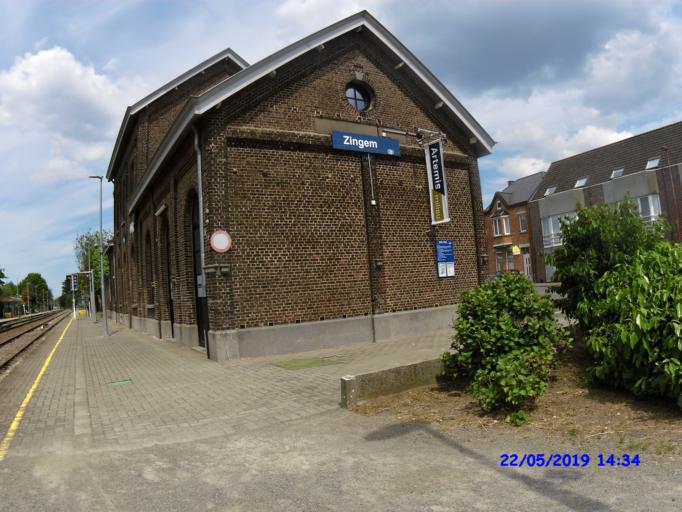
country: BE
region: Flanders
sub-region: Provincie Oost-Vlaanderen
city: Zingem
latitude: 50.9078
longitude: 3.6464
